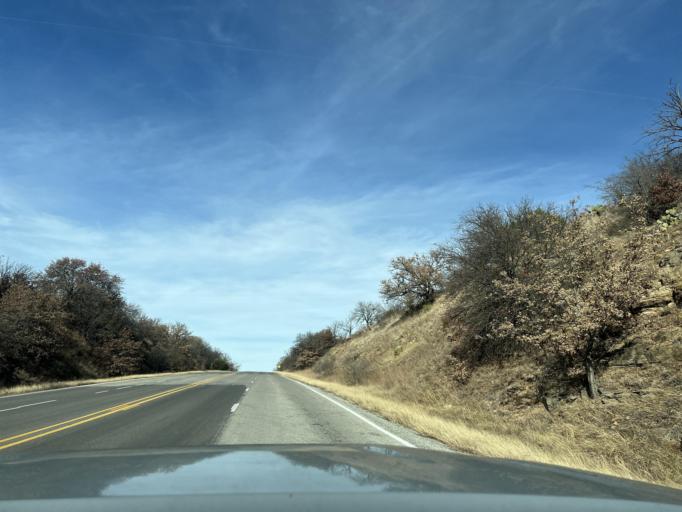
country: US
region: Texas
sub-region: Eastland County
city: Cisco
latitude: 32.4407
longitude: -98.9802
